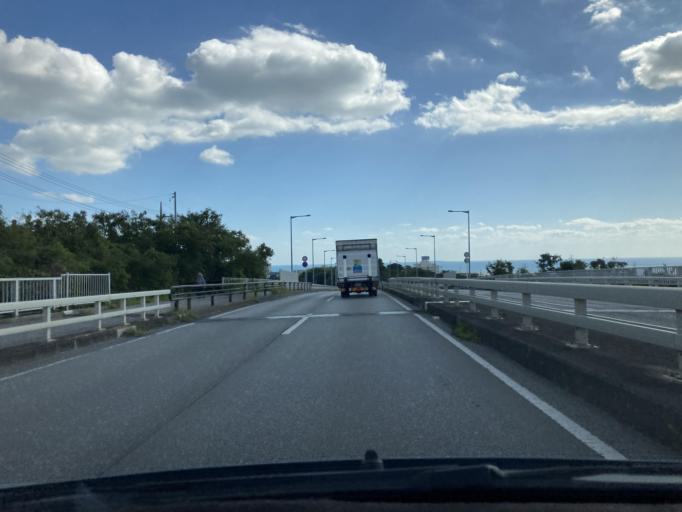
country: JP
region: Okinawa
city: Okinawa
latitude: 26.3155
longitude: 127.8022
